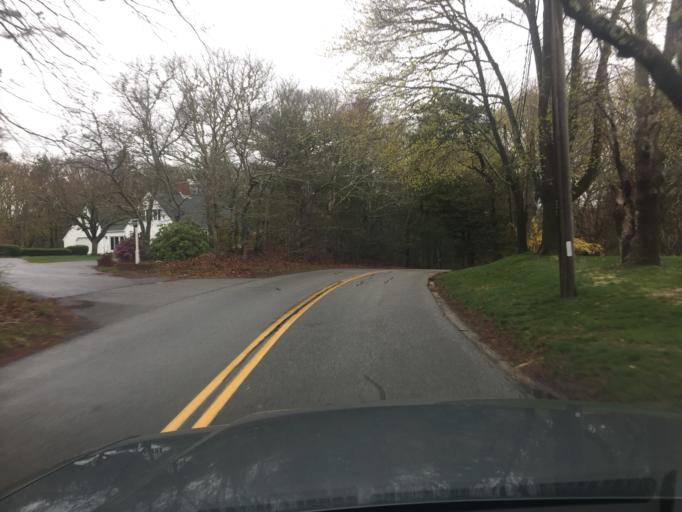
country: US
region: Massachusetts
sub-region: Barnstable County
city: North Falmouth
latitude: 41.6533
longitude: -70.6153
